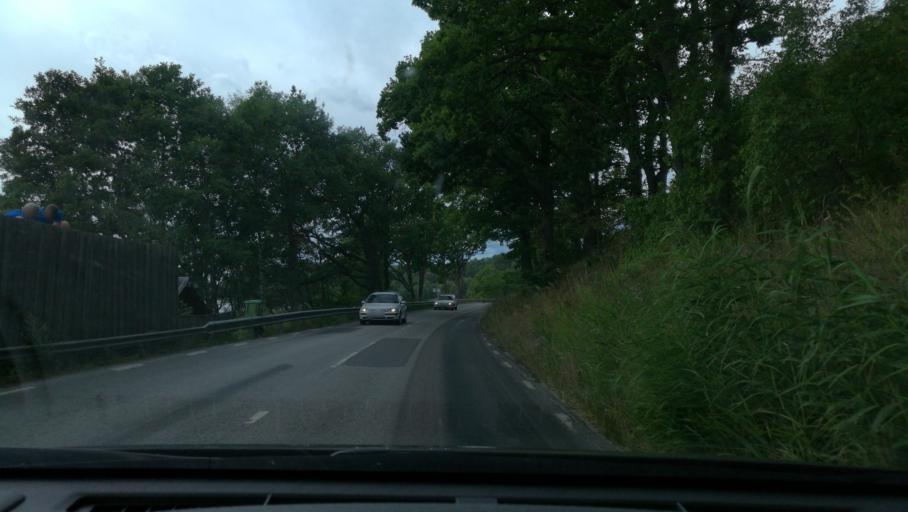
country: SE
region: OEstergoetland
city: Lindo
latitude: 58.6664
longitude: 16.2889
